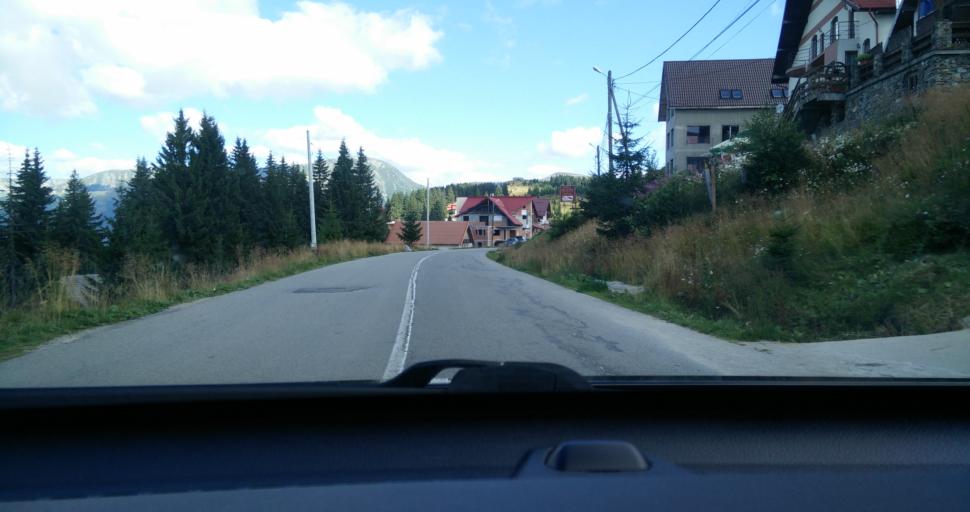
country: RO
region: Gorj
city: Novaci-Straini
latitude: 45.2896
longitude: 23.6898
